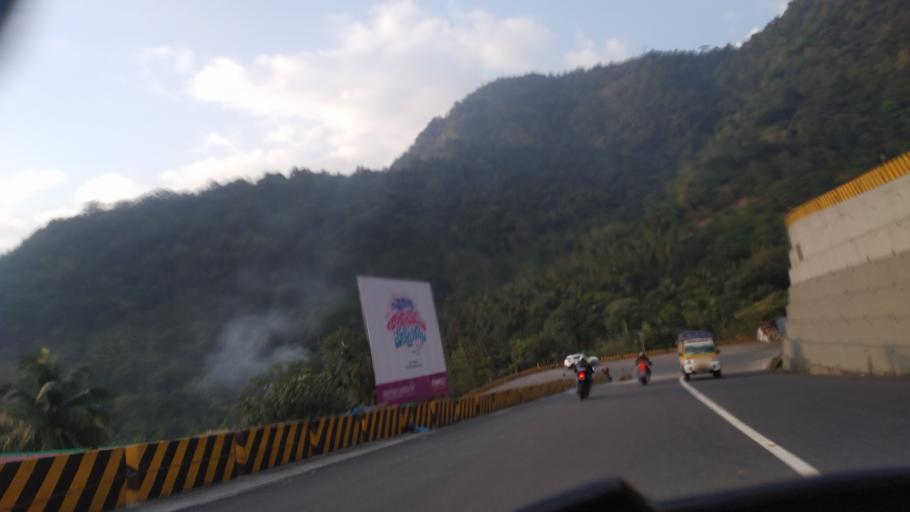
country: IN
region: Kerala
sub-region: Wayanad
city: Kalpetta
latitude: 11.5027
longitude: 76.0238
